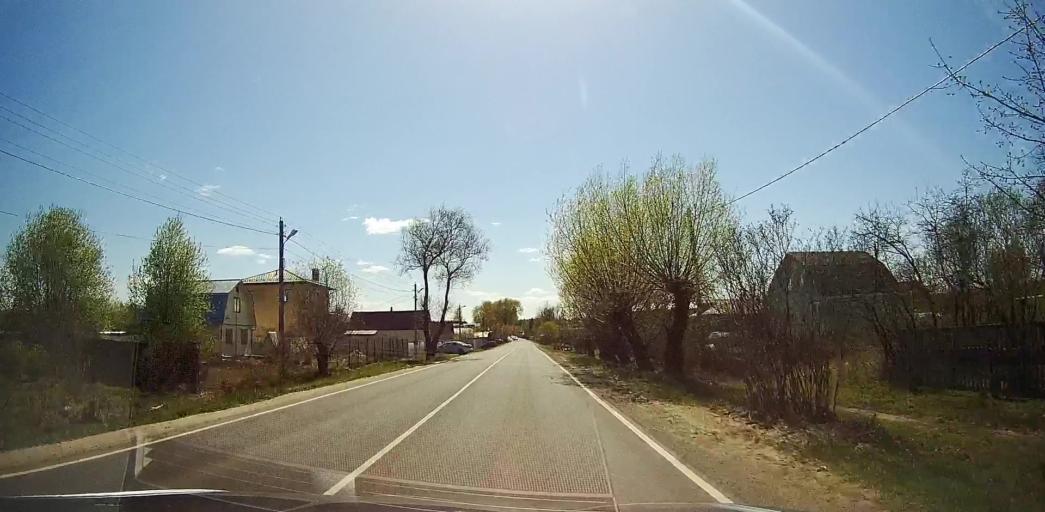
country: RU
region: Moskovskaya
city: Beloozerskiy
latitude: 55.5100
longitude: 38.4314
